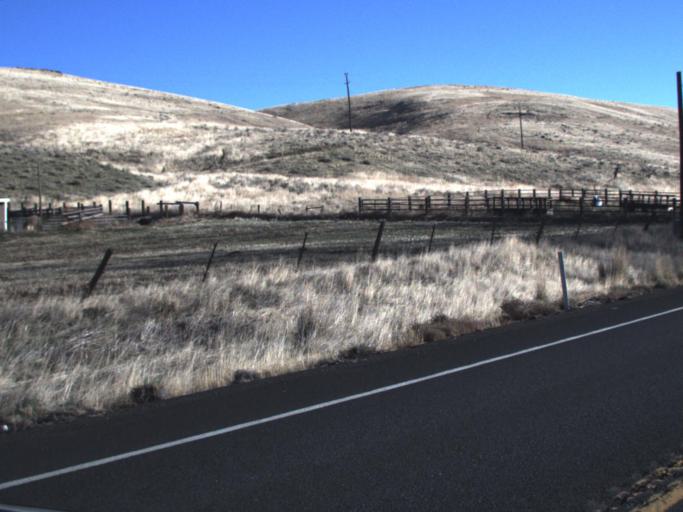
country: US
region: Washington
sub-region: Garfield County
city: Pomeroy
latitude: 46.4748
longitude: -117.5630
